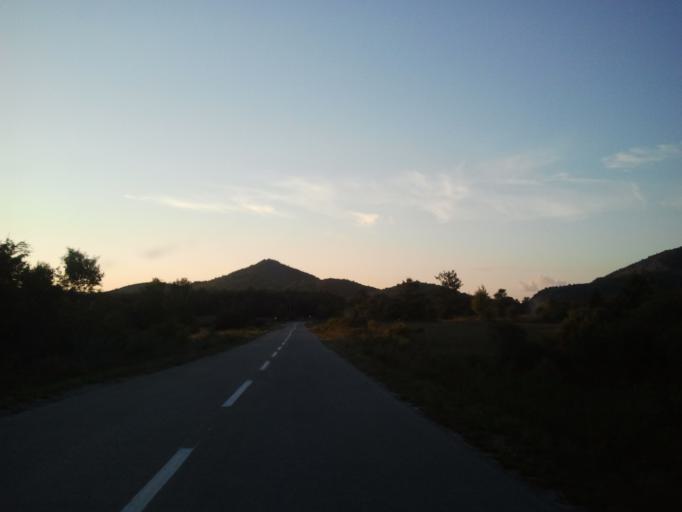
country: HR
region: Zadarska
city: Obrovac
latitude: 44.4178
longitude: 15.6624
